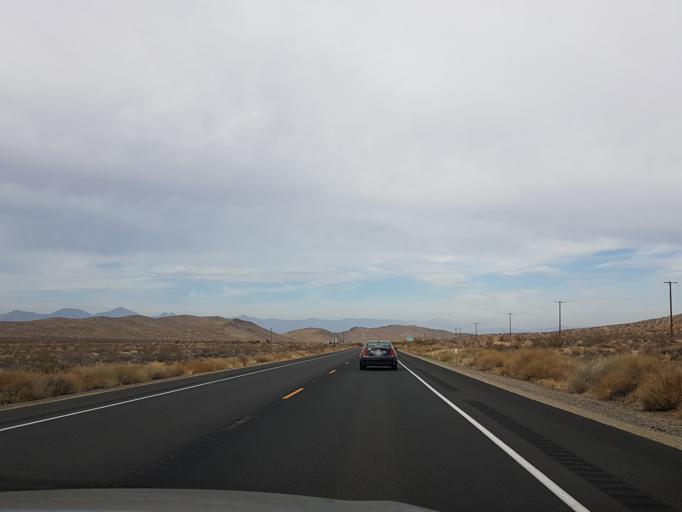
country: US
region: California
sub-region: Kern County
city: Ridgecrest
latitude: 35.5233
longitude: -117.6750
